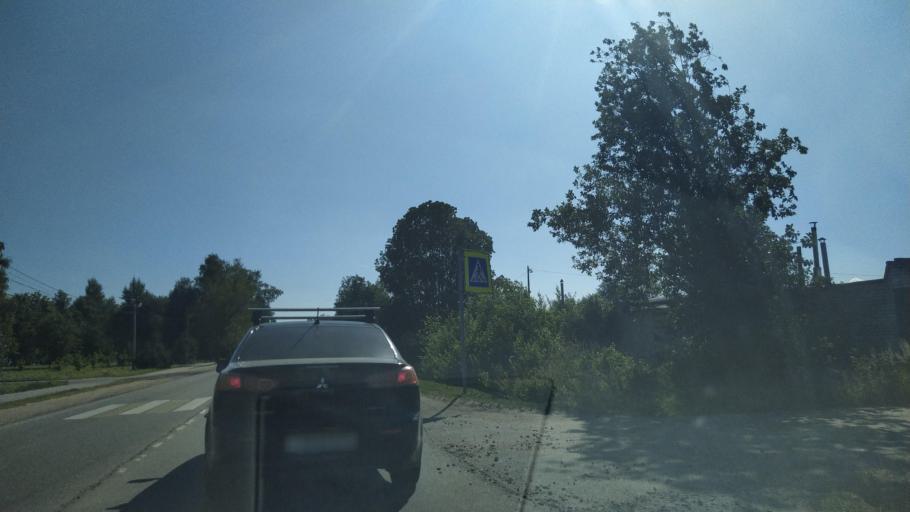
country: RU
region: Leningrad
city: Imeni Morozova
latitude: 59.9775
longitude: 31.0344
